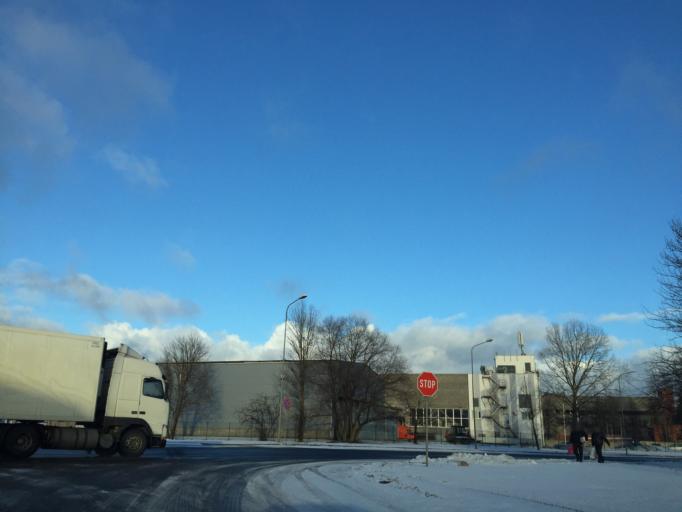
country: LV
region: Riga
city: Riga
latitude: 56.9889
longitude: 24.1129
